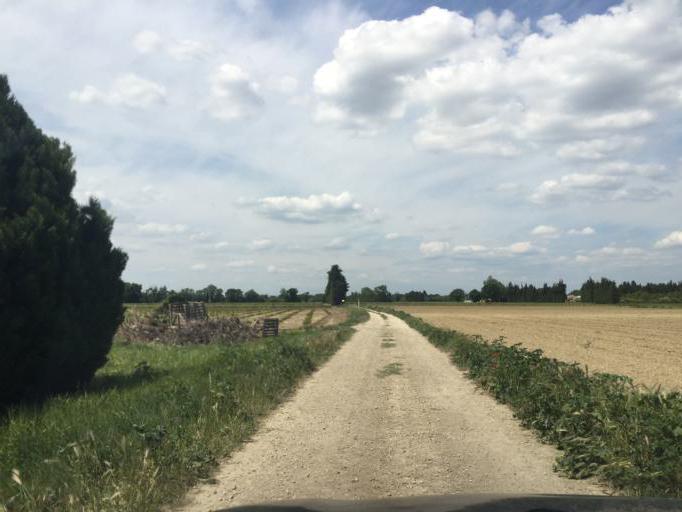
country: FR
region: Provence-Alpes-Cote d'Azur
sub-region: Departement du Vaucluse
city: Jonquieres
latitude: 44.1334
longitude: 4.9085
